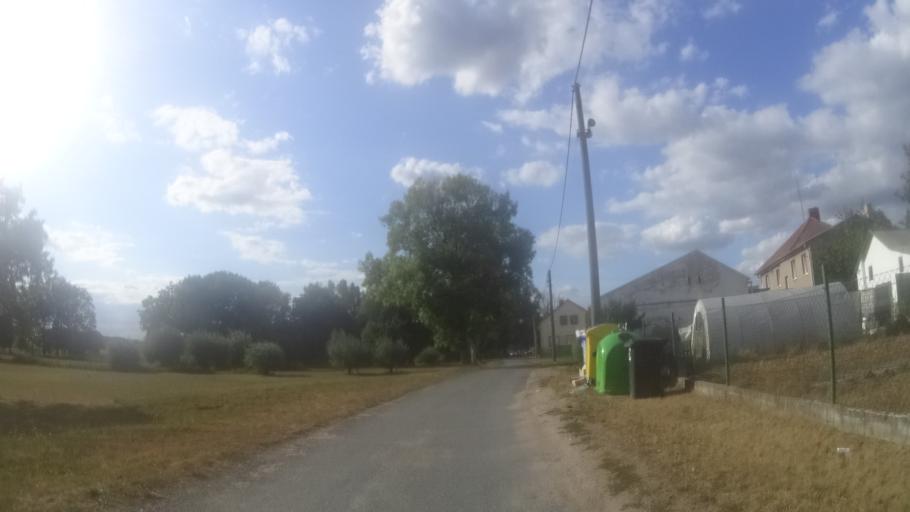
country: CZ
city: Albrechtice nad Orlici
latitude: 50.1669
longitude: 16.0318
